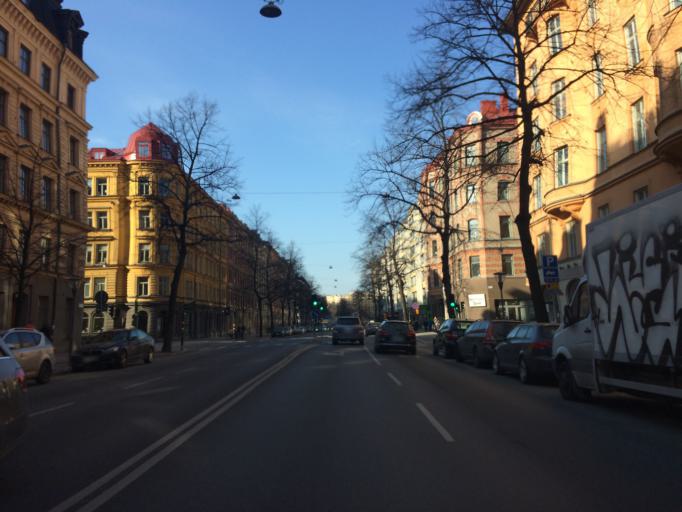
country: SE
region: Stockholm
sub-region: Stockholms Kommun
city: Stockholm
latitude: 59.3478
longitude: 18.0606
